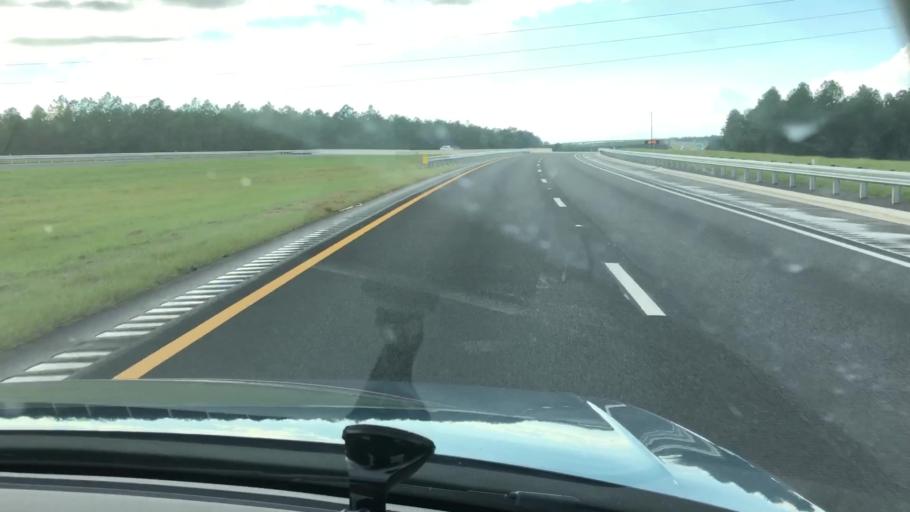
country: US
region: Florida
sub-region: Lake County
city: Mount Plymouth
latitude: 28.7764
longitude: -81.5308
